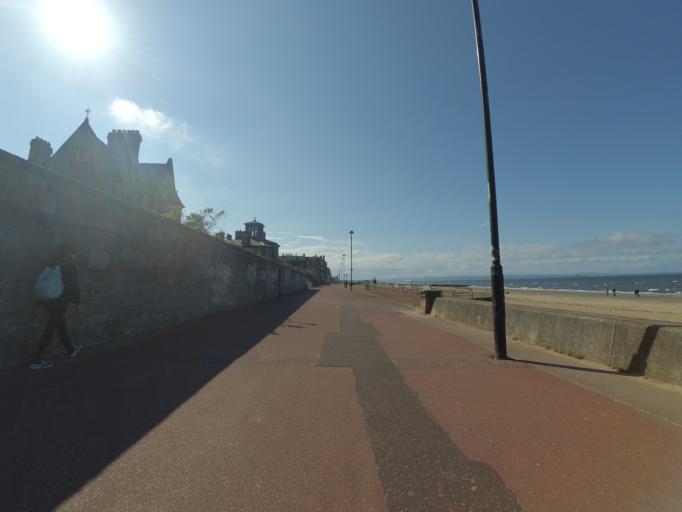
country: GB
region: Scotland
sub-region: East Lothian
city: Musselburgh
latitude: 55.9509
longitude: -3.1006
